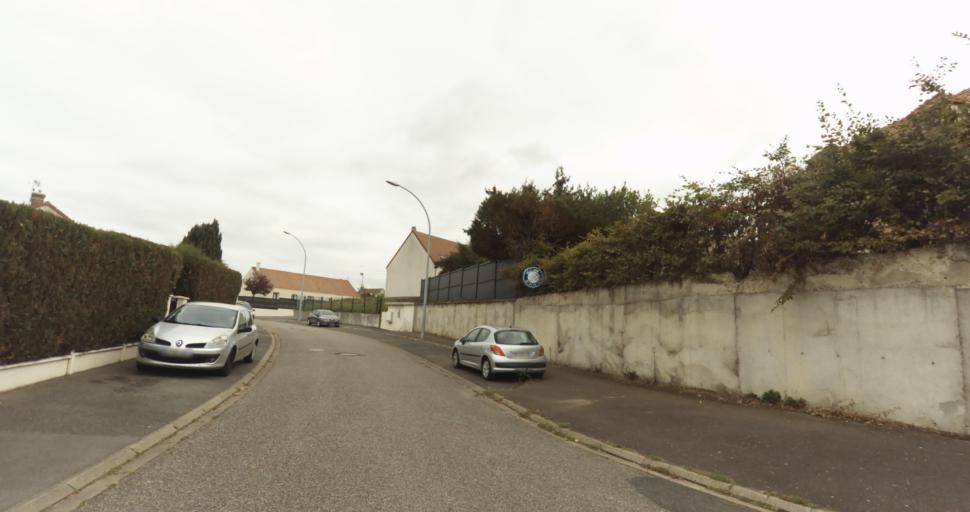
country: FR
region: Centre
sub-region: Departement d'Eure-et-Loir
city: Vernouillet
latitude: 48.7168
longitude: 1.3575
